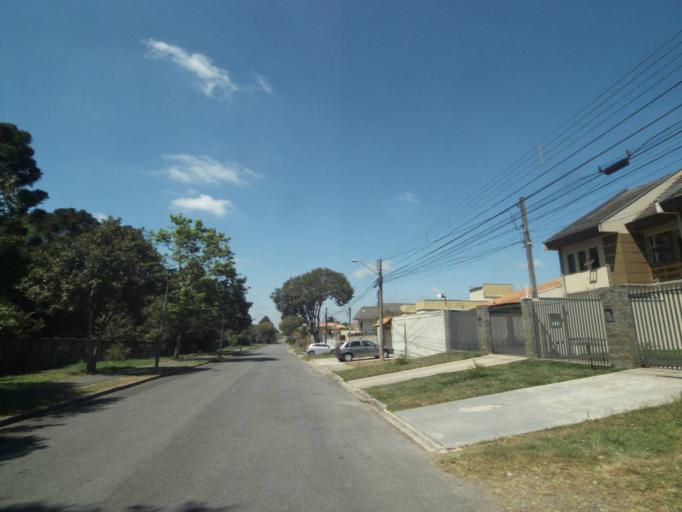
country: BR
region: Parana
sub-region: Sao Jose Dos Pinhais
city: Sao Jose dos Pinhais
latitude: -25.5097
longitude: -49.2390
